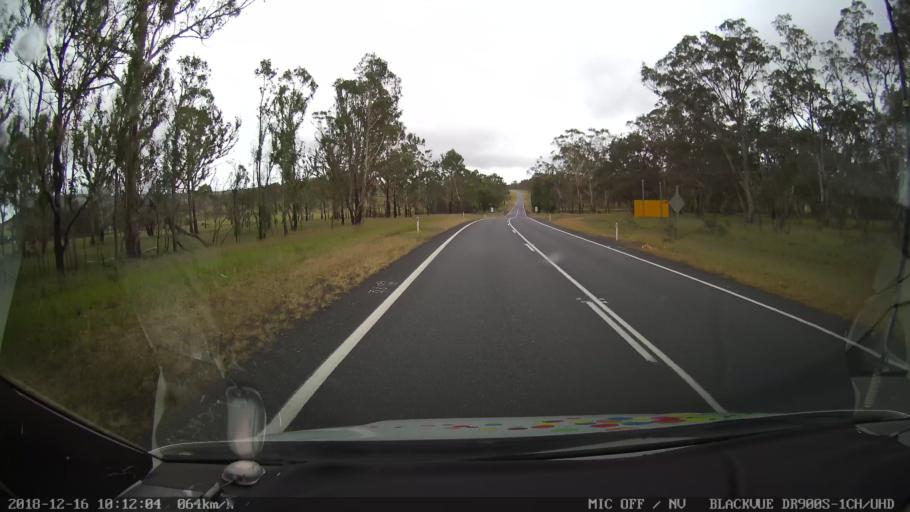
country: AU
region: New South Wales
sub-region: Glen Innes Severn
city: Glen Innes
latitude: -29.3083
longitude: 151.9368
